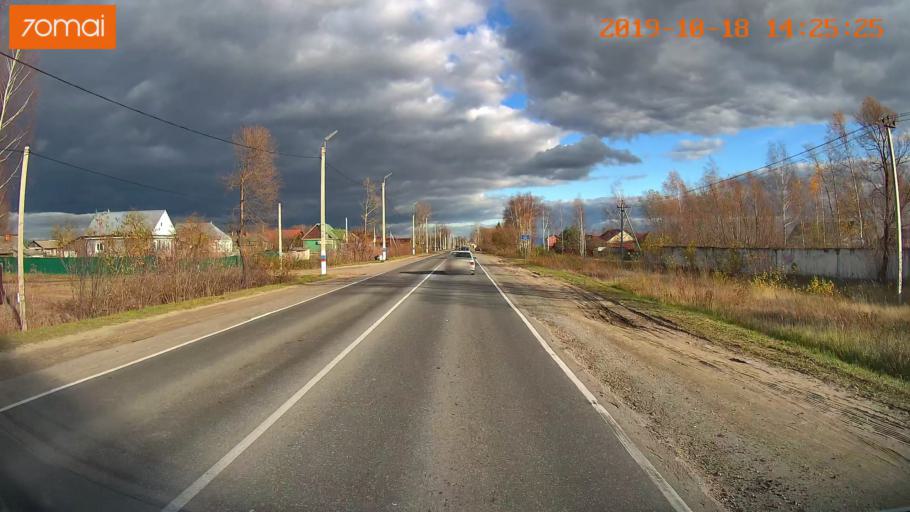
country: RU
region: Rjazan
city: Tuma
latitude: 55.1468
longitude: 40.5174
